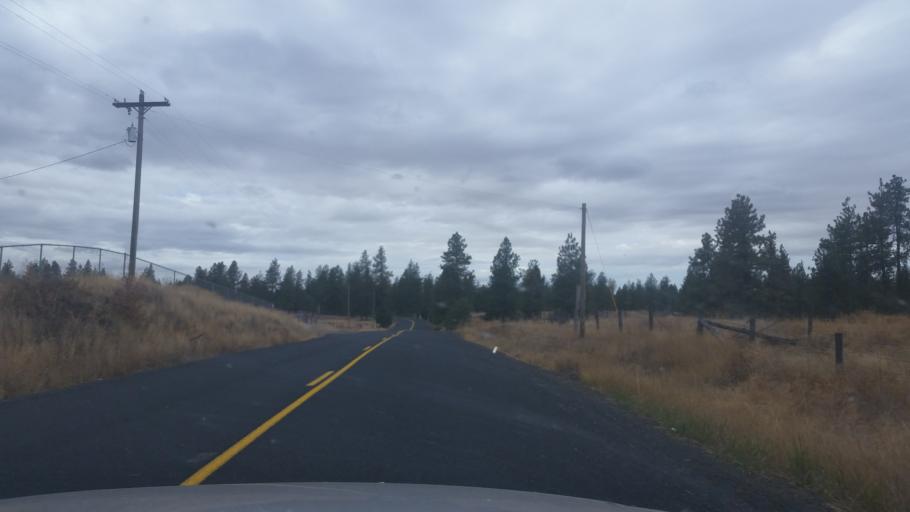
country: US
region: Washington
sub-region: Spokane County
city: Medical Lake
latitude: 47.5163
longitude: -117.7469
